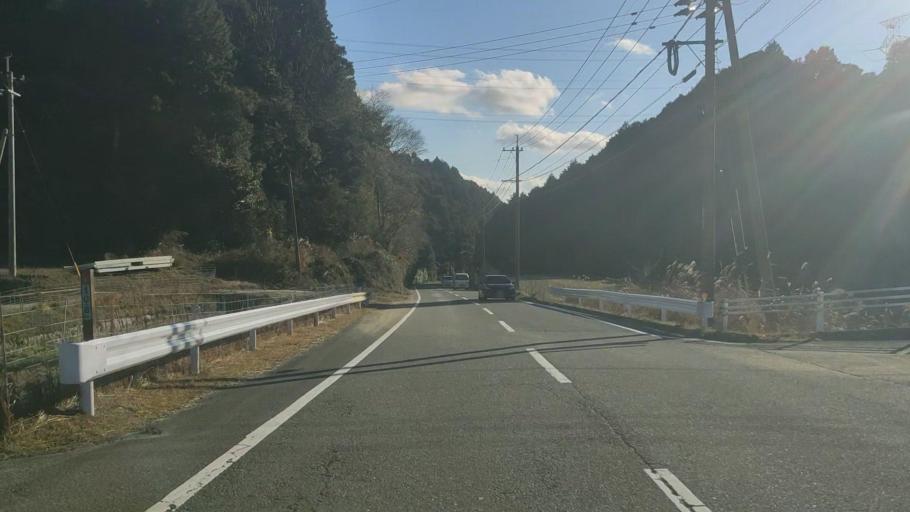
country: JP
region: Saga Prefecture
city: Kanzakimachi-kanzaki
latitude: 33.3991
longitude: 130.2716
